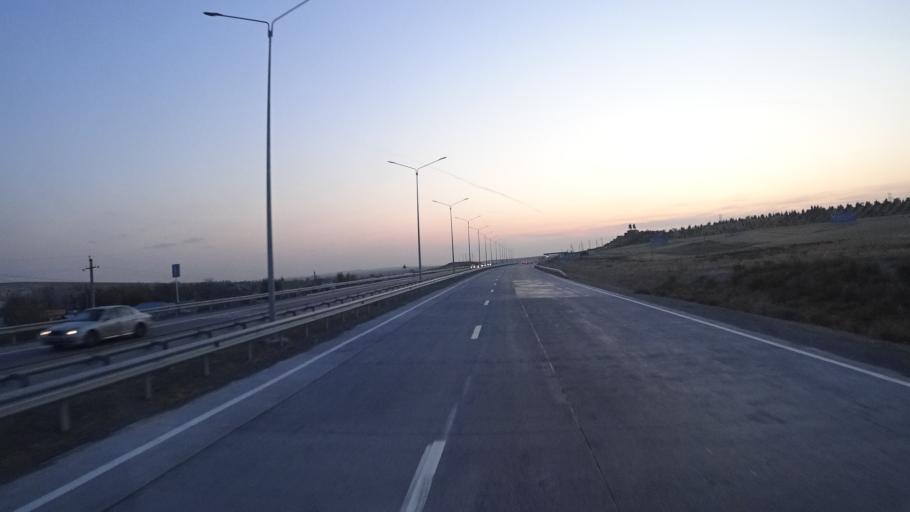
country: KZ
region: Ongtustik Qazaqstan
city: Qazyqurt
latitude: 41.8767
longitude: 69.4316
